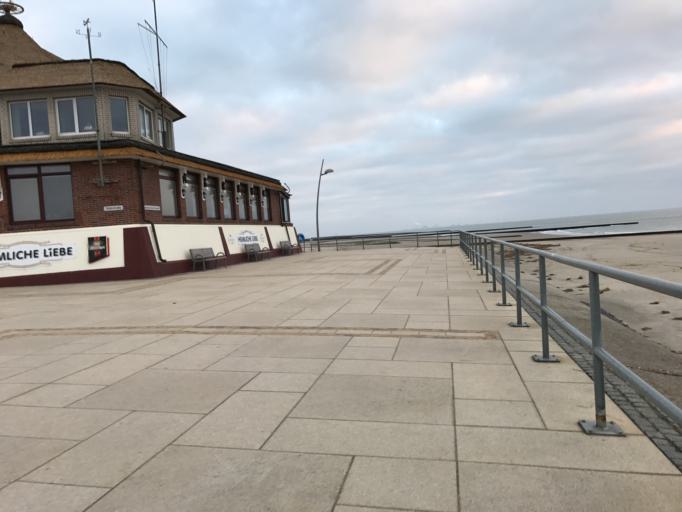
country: DE
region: Lower Saxony
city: Borkum
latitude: 53.5784
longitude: 6.6649
